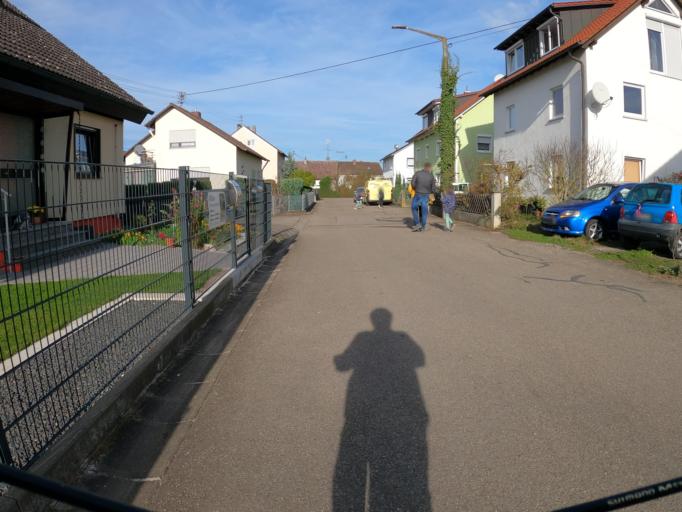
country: DE
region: Bavaria
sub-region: Swabia
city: Leipheim
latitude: 48.4005
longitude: 10.1997
